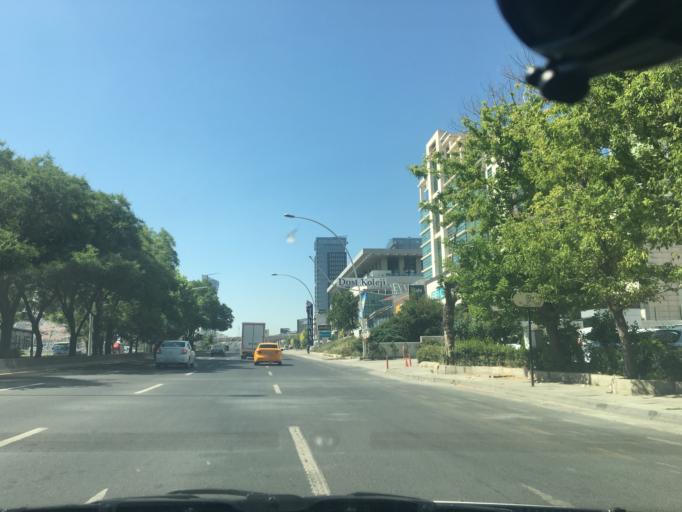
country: TR
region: Ankara
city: Ankara
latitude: 39.8911
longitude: 32.8127
